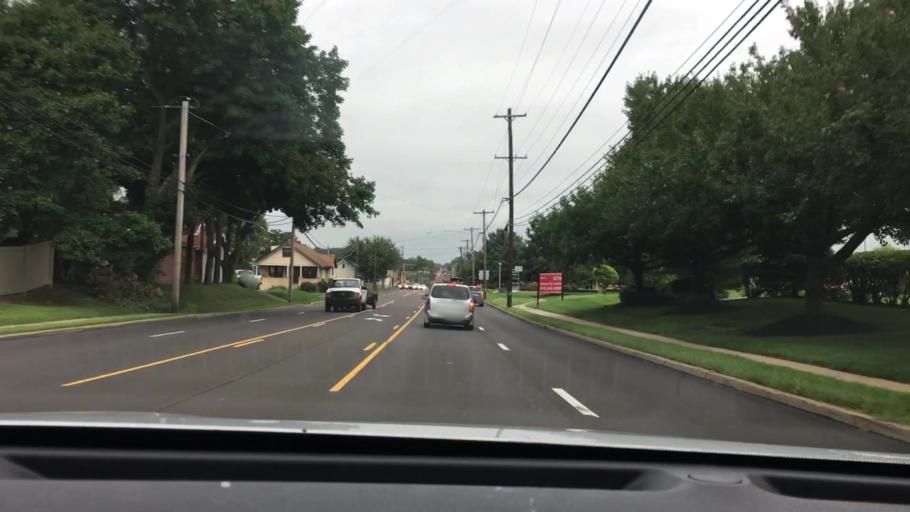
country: US
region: Pennsylvania
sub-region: Bucks County
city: Warminster Heights
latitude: 40.1834
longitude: -75.0917
